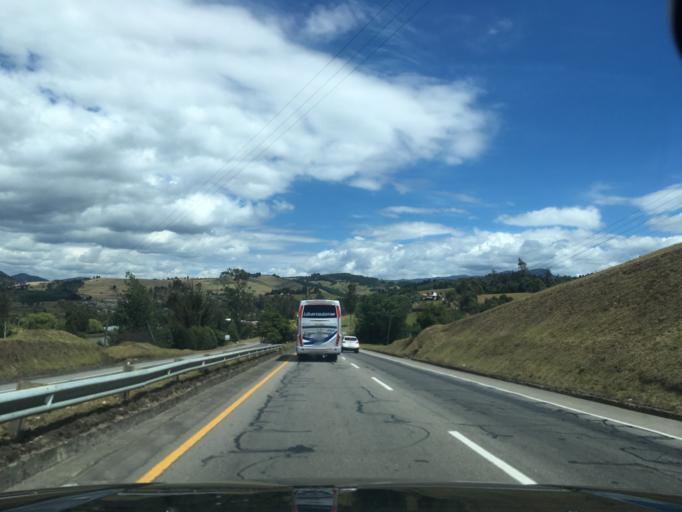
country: CO
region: Cundinamarca
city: Choconta
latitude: 5.1016
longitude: -73.7074
